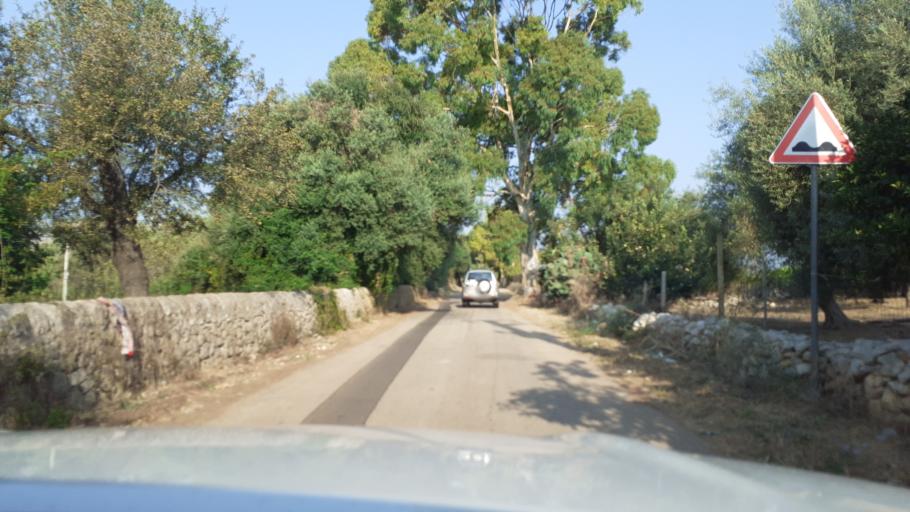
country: IT
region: Sicily
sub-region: Provincia di Siracusa
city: Cassibile
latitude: 36.9743
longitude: 15.1889
